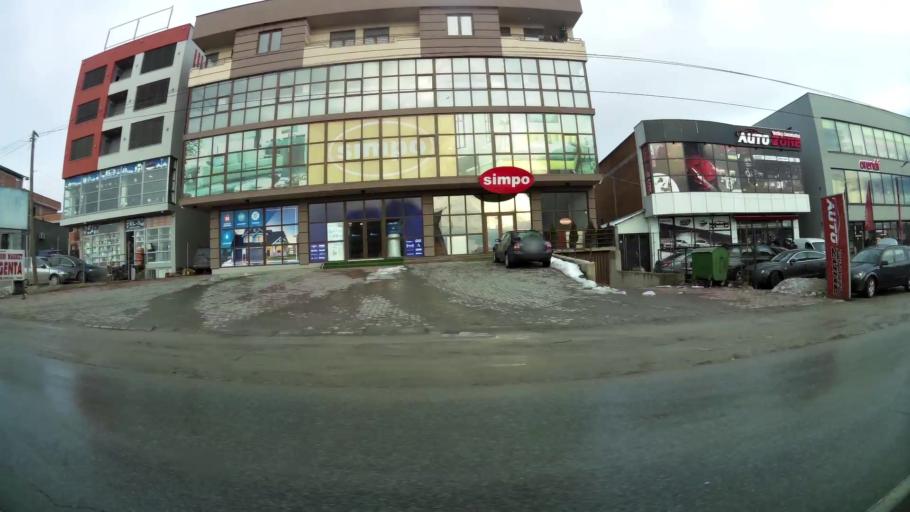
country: XK
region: Pristina
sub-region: Komuna e Prishtines
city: Pristina
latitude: 42.6270
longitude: 21.1611
